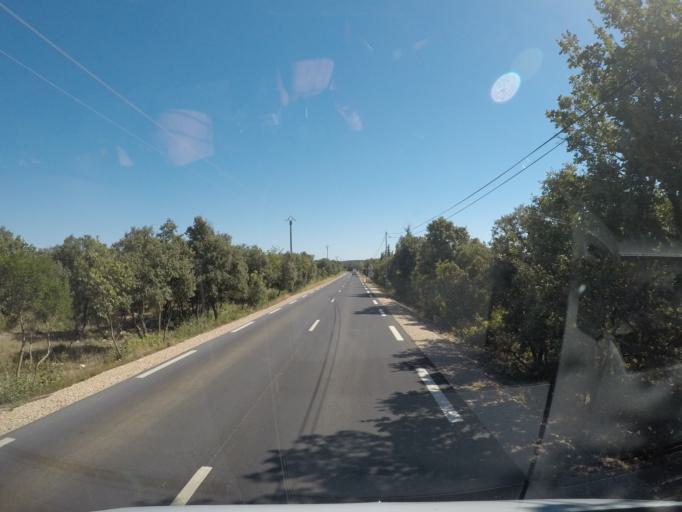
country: FR
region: Languedoc-Roussillon
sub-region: Departement de l'Herault
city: Aniane
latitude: 43.7274
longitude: 3.6458
